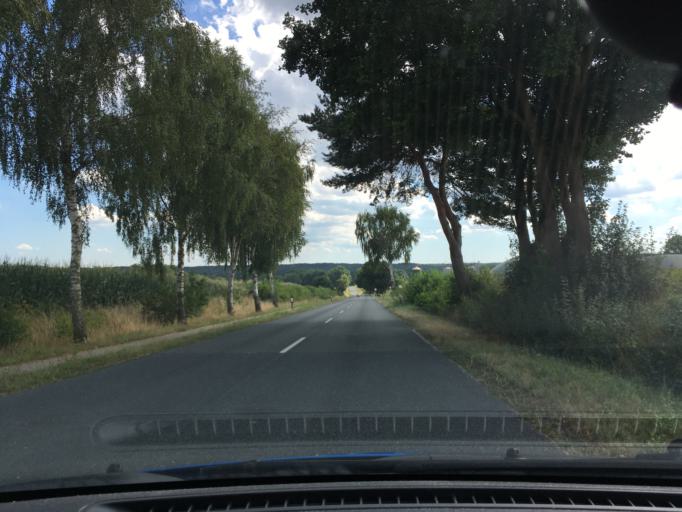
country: DE
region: Lower Saxony
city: Amelinghausen
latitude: 53.1162
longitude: 10.2170
